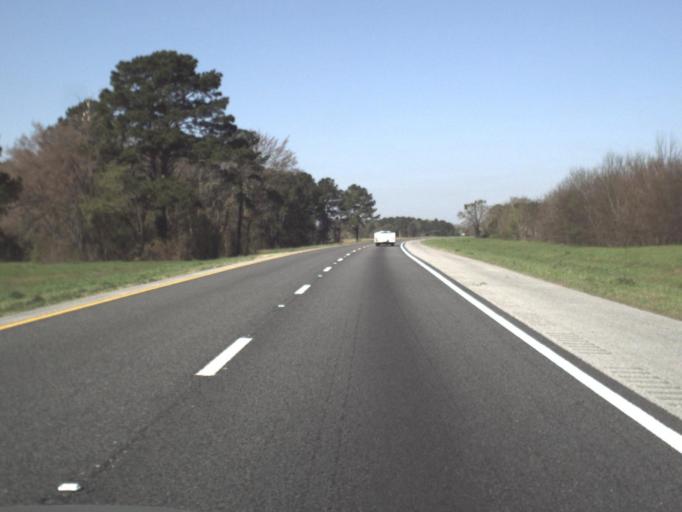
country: US
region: Florida
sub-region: Jackson County
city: Sneads
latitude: 30.6404
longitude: -84.9955
